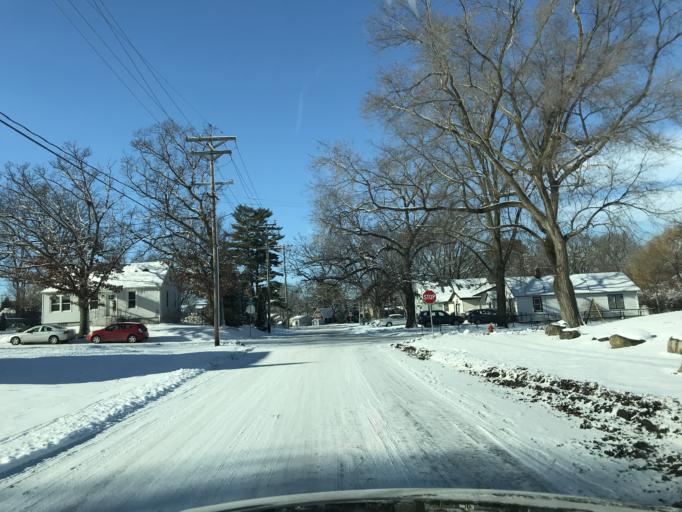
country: US
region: Wisconsin
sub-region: Dane County
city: Monona
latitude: 43.0813
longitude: -89.3145
